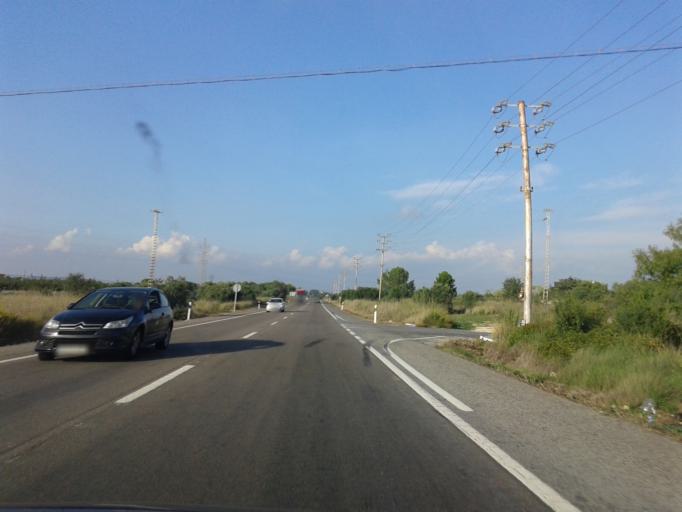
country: ES
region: Catalonia
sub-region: Provincia de Barcelona
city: Castellet
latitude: 41.2777
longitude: 1.6119
